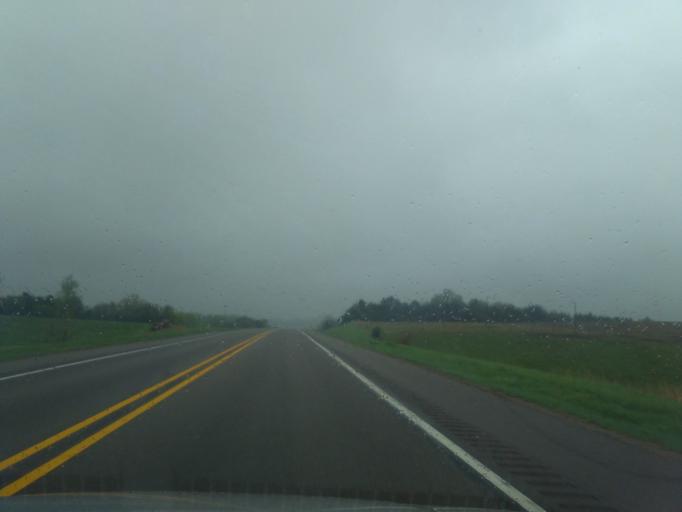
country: US
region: Nebraska
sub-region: Madison County
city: Norfolk
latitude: 42.0968
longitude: -97.3180
